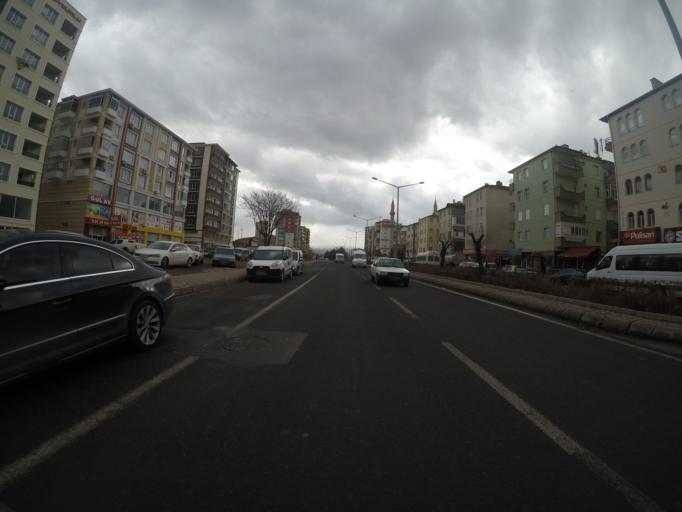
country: TR
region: Kayseri
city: Melikgazi
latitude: 38.7548
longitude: 35.4684
